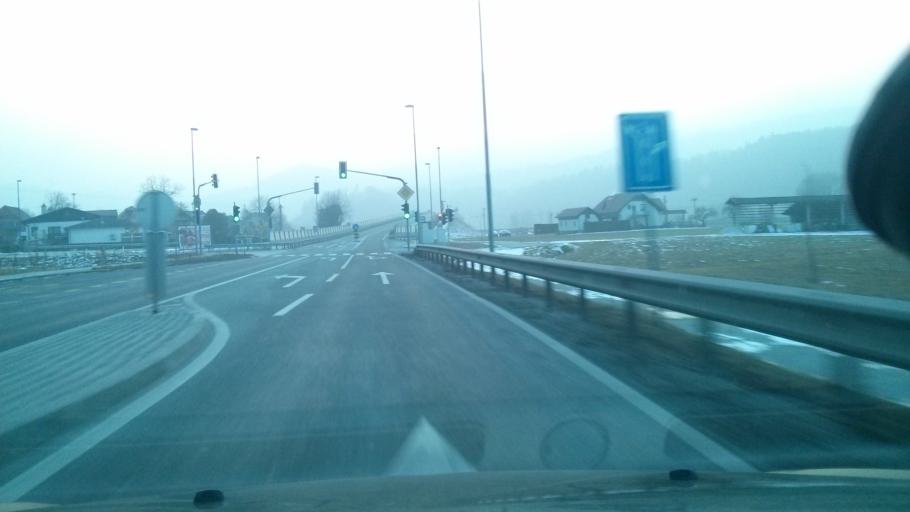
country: SI
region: Litija
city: Litija
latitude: 46.0807
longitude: 14.8291
